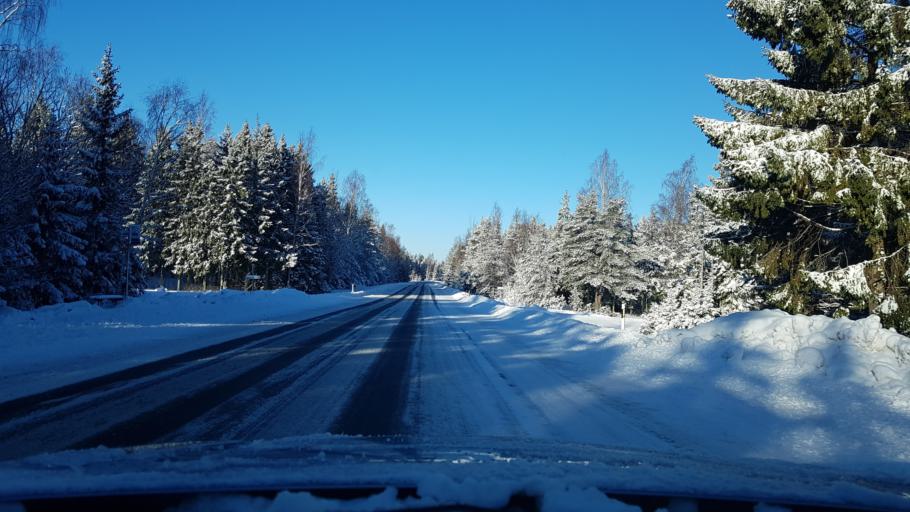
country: EE
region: Hiiumaa
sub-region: Kaerdla linn
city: Kardla
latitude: 58.9760
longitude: 22.8171
